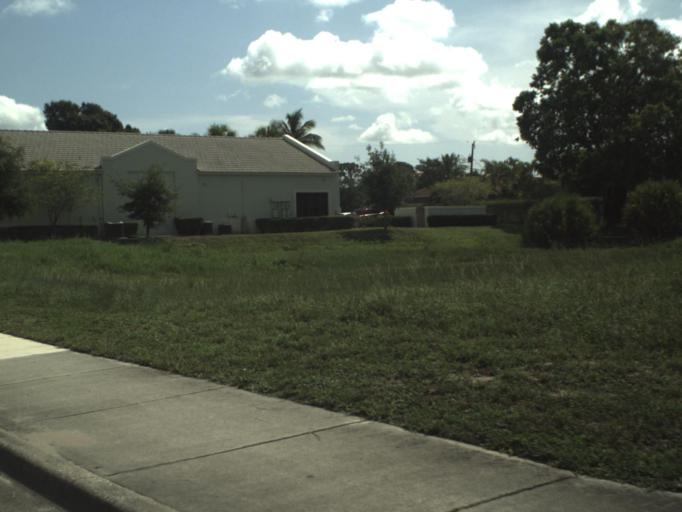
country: US
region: Florida
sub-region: Saint Lucie County
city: Port Saint Lucie
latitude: 27.2630
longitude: -80.3727
